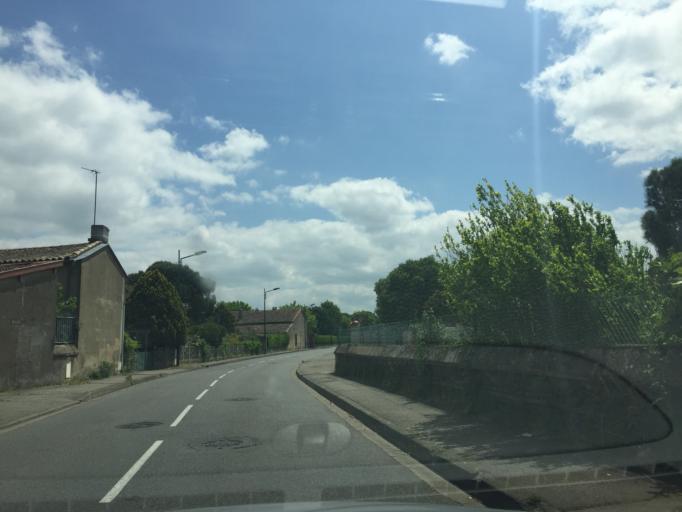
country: FR
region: Midi-Pyrenees
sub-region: Departement de la Haute-Garonne
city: Aucamville
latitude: 43.6440
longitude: 1.4443
